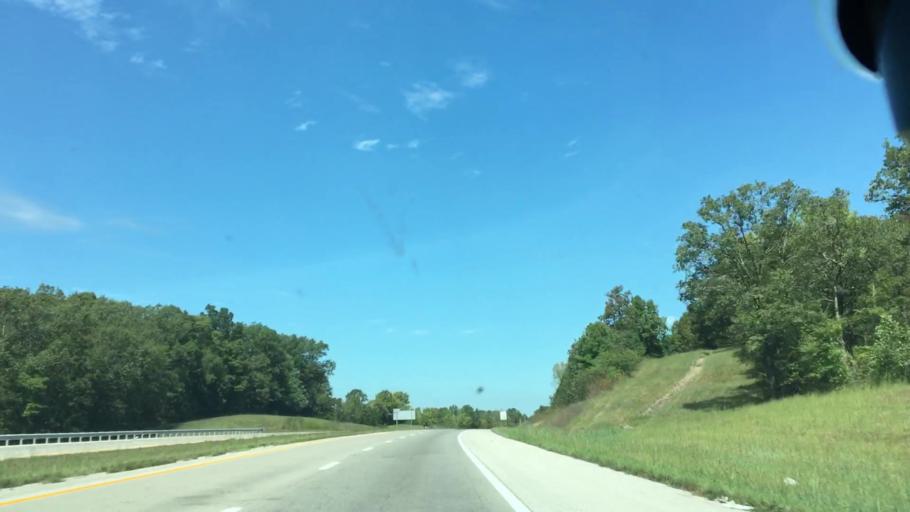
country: US
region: Kentucky
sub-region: Christian County
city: Hopkinsville
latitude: 36.9054
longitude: -87.4727
